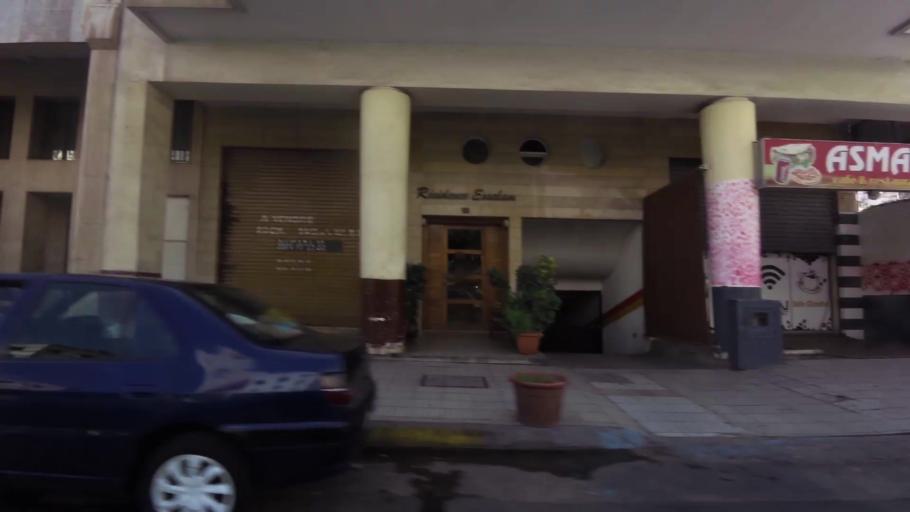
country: MA
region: Grand Casablanca
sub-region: Casablanca
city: Casablanca
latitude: 33.5997
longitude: -7.6363
